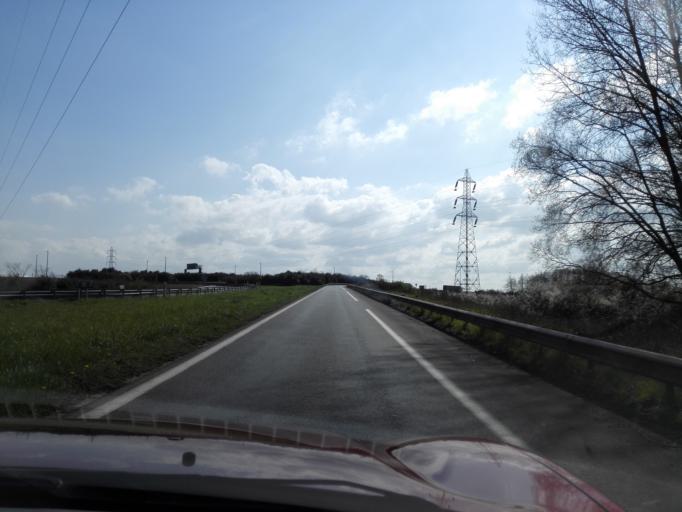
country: FR
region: Nord-Pas-de-Calais
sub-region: Departement du Nord
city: Grande-Synthe
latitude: 51.0010
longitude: 2.2888
